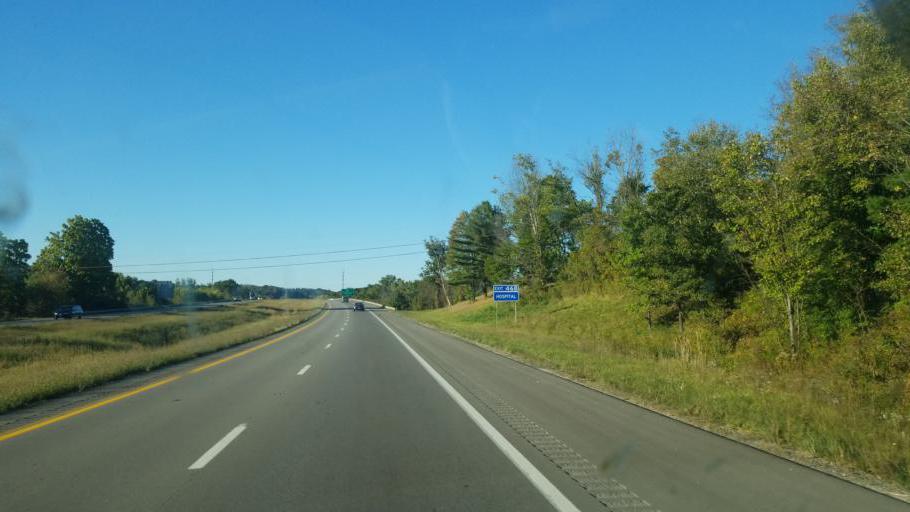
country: US
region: Ohio
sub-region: Guernsey County
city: Cambridge
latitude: 40.0144
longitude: -81.5590
